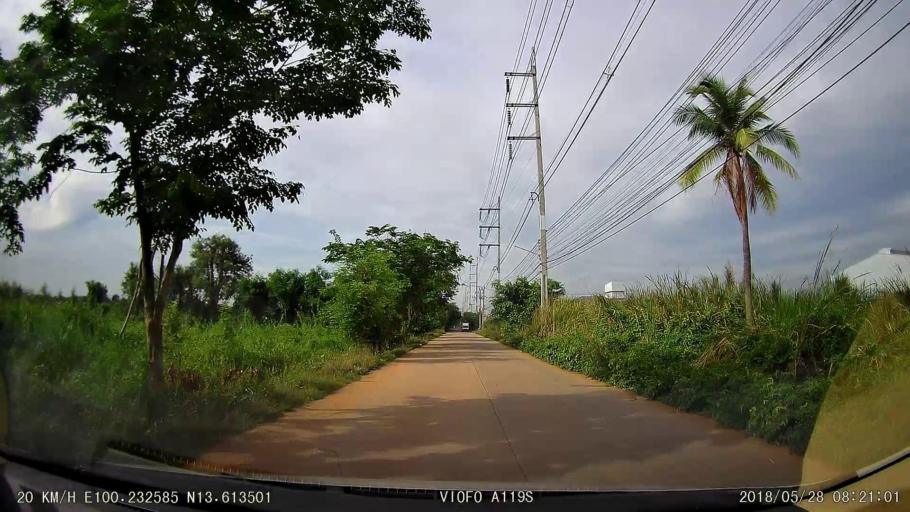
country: TH
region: Samut Sakhon
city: Krathum Baen
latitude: 13.6133
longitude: 100.2326
